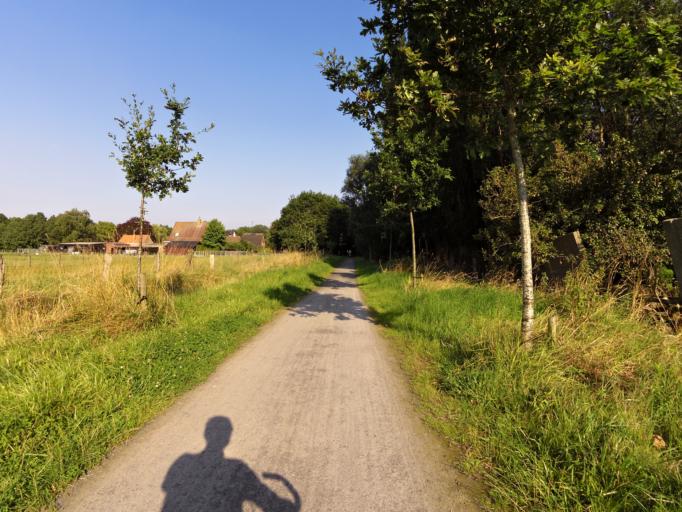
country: BE
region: Flanders
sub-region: Provincie West-Vlaanderen
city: Ichtegem
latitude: 51.1292
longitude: 3.0100
